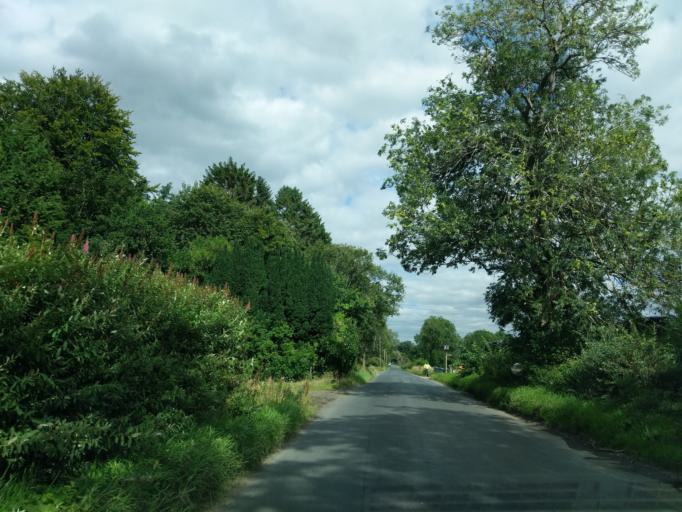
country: GB
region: Scotland
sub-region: The Scottish Borders
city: Peebles
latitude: 55.6229
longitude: -3.3006
